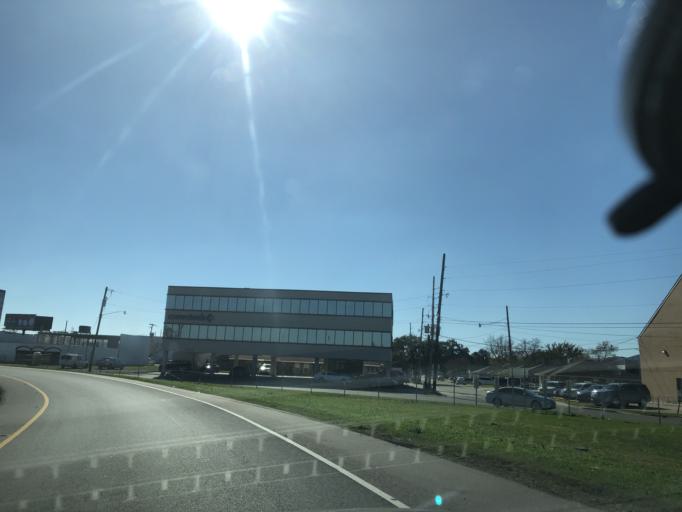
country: US
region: Louisiana
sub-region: Jefferson Parish
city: Metairie
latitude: 29.9962
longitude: -90.1575
